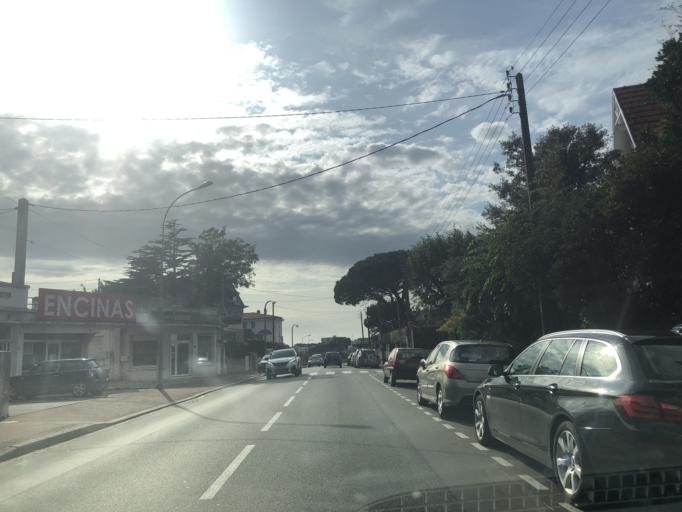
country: FR
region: Poitou-Charentes
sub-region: Departement de la Charente-Maritime
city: Royan
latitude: 45.6250
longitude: -1.0473
